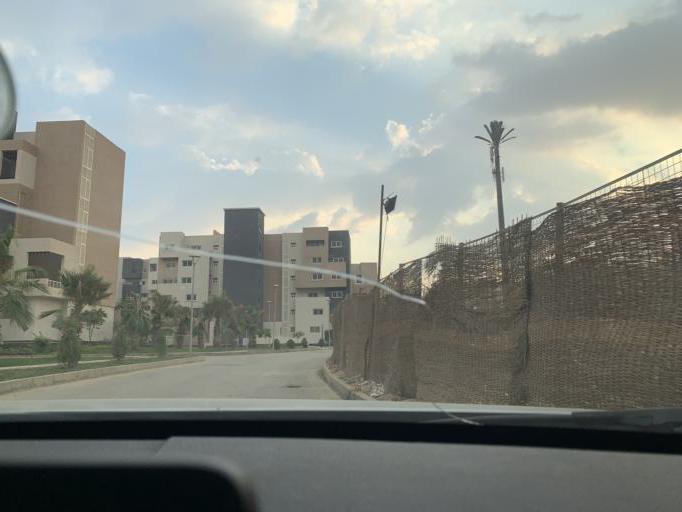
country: EG
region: Muhafazat al Qalyubiyah
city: Al Khankah
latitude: 30.1000
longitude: 31.6521
